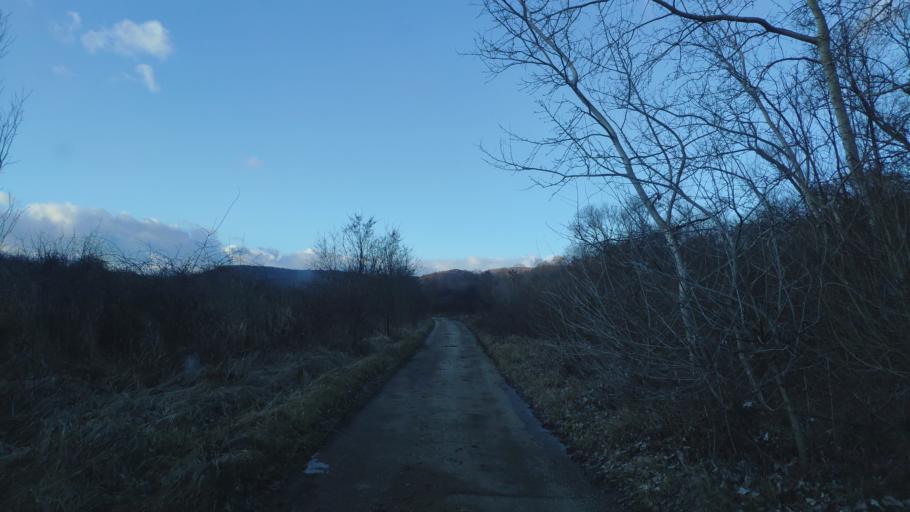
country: HU
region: Borsod-Abauj-Zemplen
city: Tolcsva
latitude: 48.2837
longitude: 21.4878
